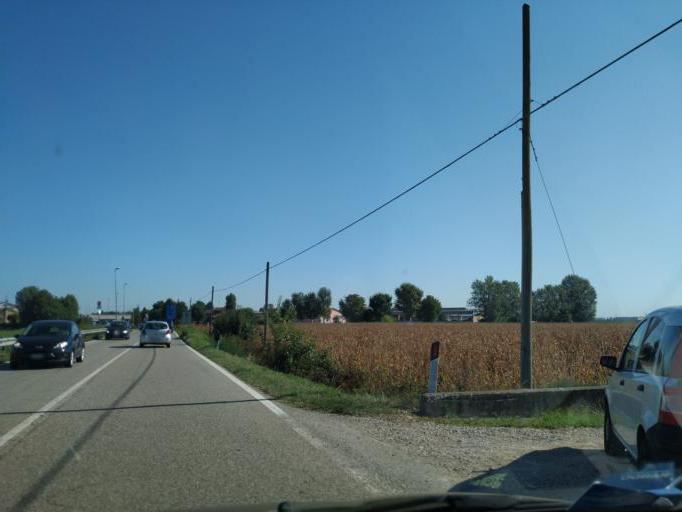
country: IT
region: Emilia-Romagna
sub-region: Provincia di Bologna
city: Decima
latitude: 44.6952
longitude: 11.2237
